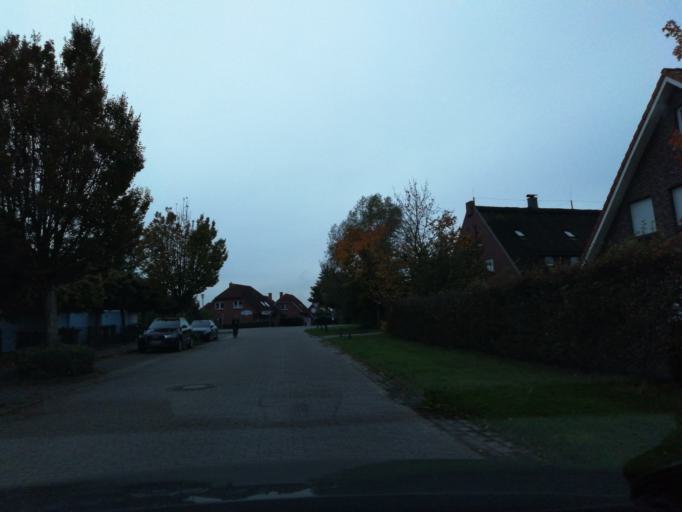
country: DE
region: Lower Saxony
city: Schillig
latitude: 53.6345
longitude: 8.0346
